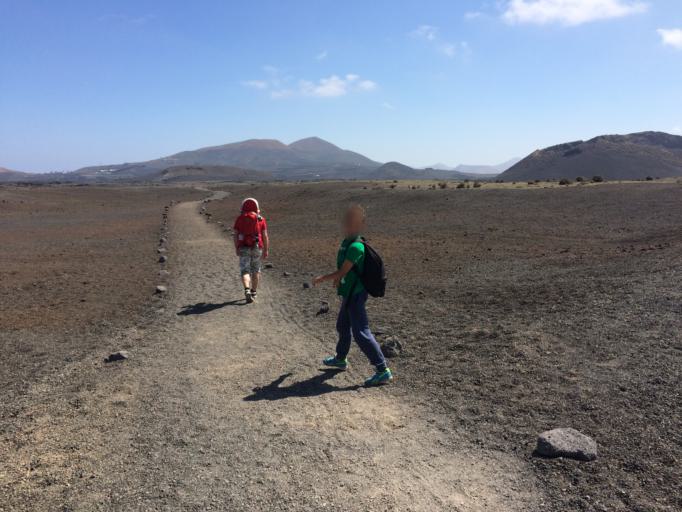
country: ES
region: Canary Islands
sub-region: Provincia de Las Palmas
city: Tias
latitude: 28.9958
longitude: -13.6850
